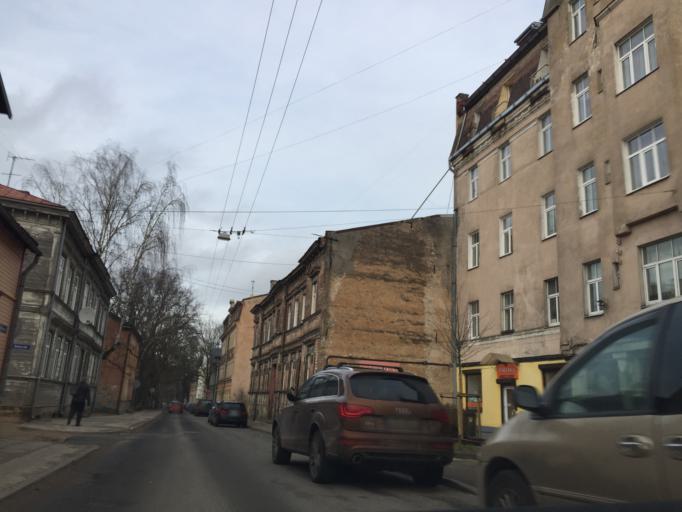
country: LV
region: Riga
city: Riga
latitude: 56.9397
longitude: 24.0788
